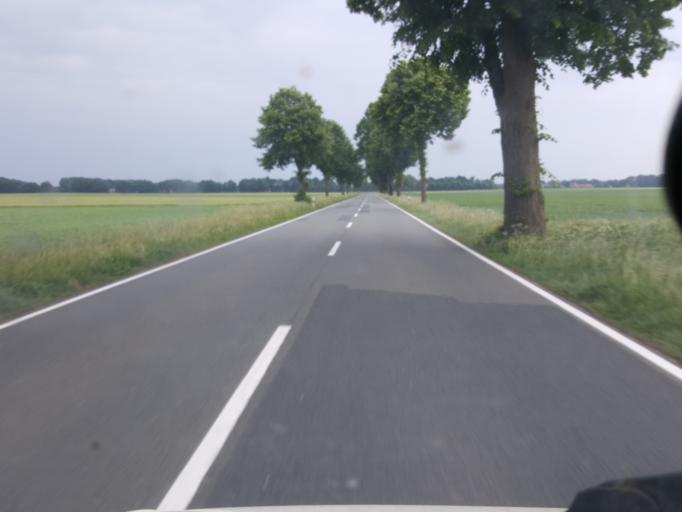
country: DE
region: Lower Saxony
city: Raddestorf
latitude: 52.4730
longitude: 8.9859
